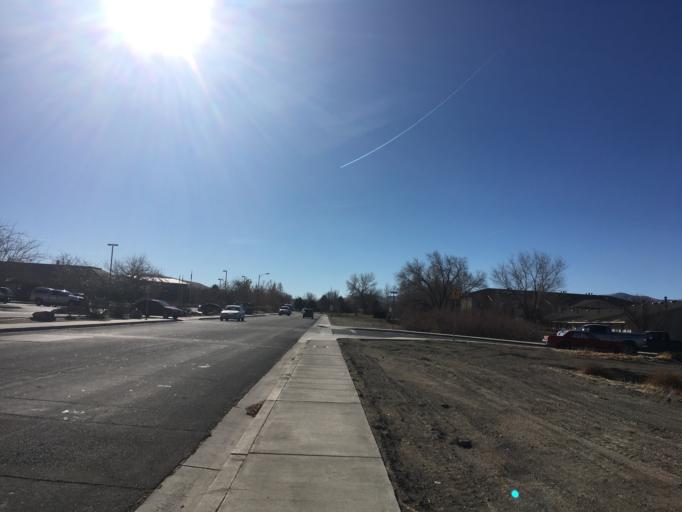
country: US
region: Nevada
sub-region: Lyon County
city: Fernley
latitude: 39.6063
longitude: -119.2413
